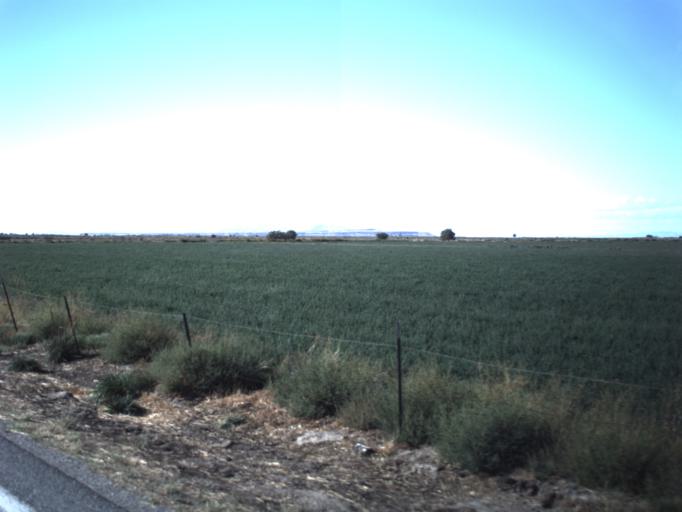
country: US
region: Utah
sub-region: Millard County
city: Delta
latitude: 39.3216
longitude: -112.6524
